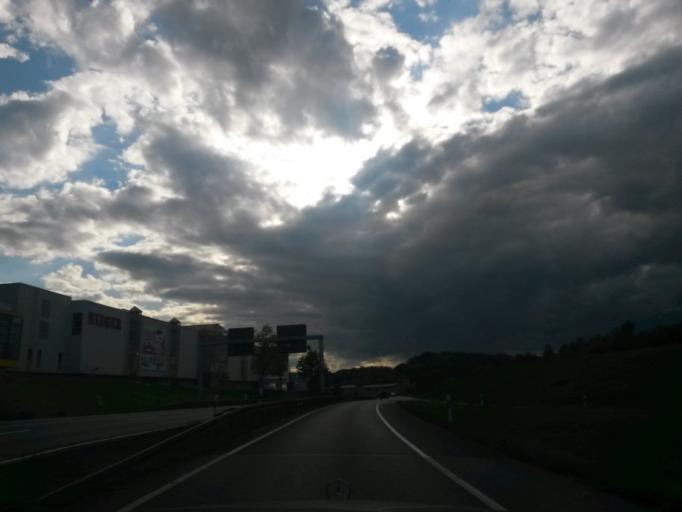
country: DE
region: Baden-Wuerttemberg
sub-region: Regierungsbezirk Stuttgart
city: Aalen
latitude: 48.8266
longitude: 10.0673
